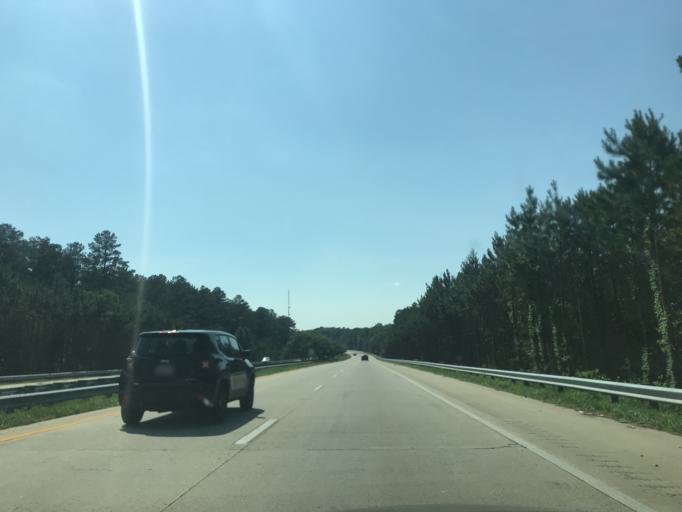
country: US
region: Maryland
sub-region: Wicomico County
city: Salisbury
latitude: 38.4034
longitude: -75.5876
